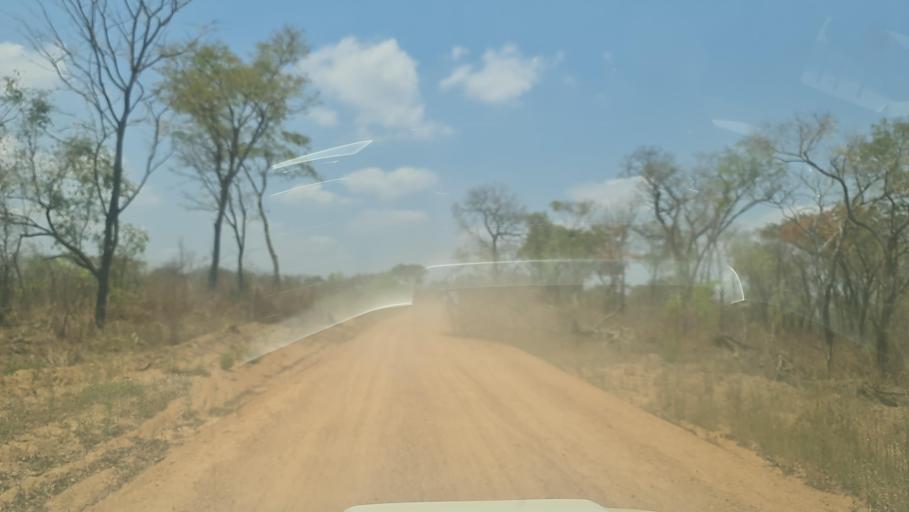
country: MW
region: Southern Region
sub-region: Nsanje District
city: Nsanje
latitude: -17.5576
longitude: 35.8974
